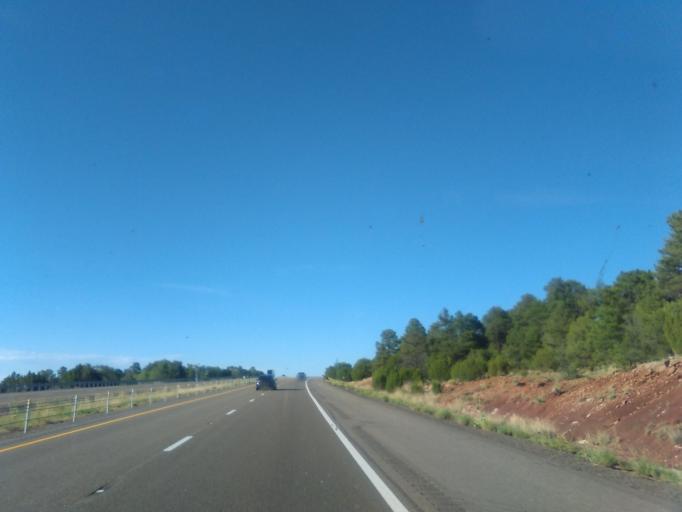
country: US
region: New Mexico
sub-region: San Miguel County
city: Las Vegas
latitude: 35.4914
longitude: -105.2697
